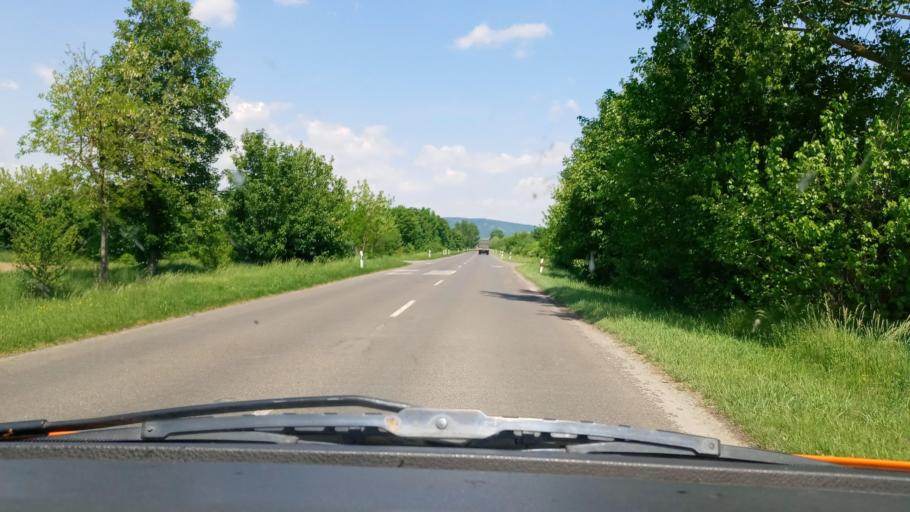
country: HU
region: Baranya
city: Harkany
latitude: 45.8278
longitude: 18.2220
